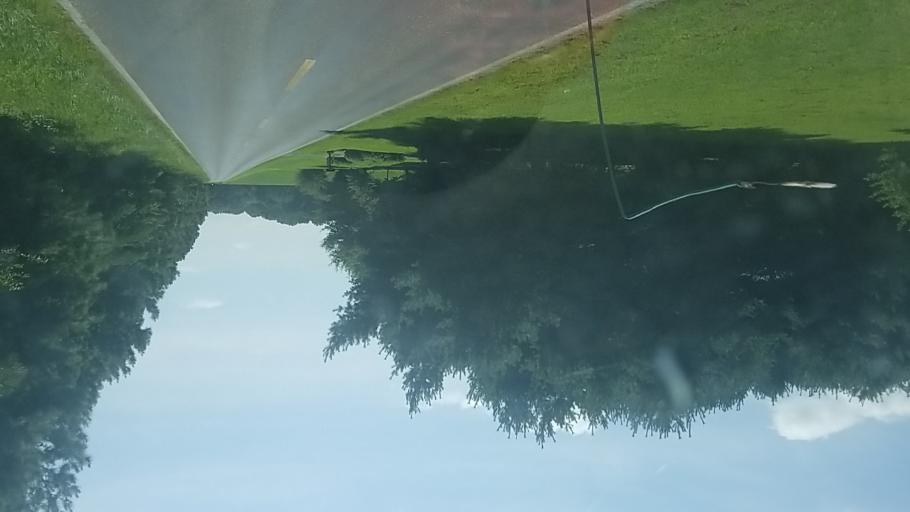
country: US
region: Maryland
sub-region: Caroline County
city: Ridgely
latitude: 38.8891
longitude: -75.9277
